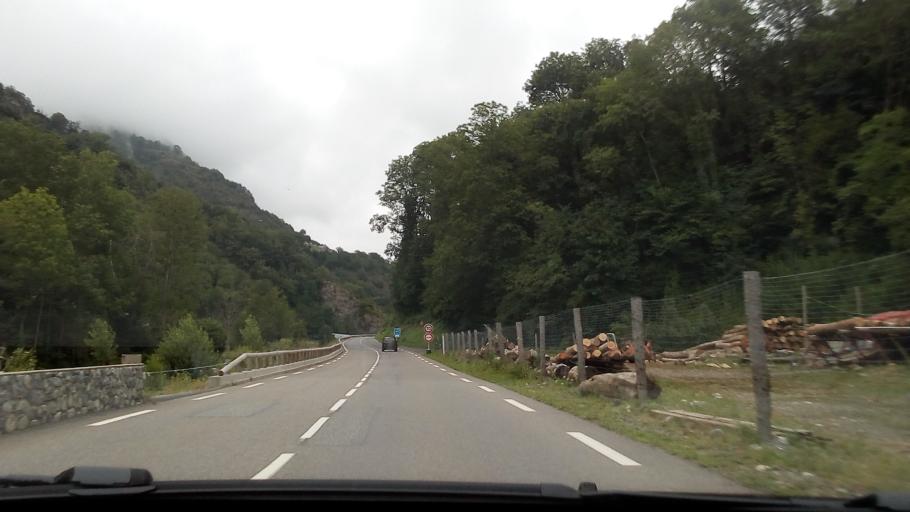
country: FR
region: Midi-Pyrenees
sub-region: Departement des Hautes-Pyrenees
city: Luz-Saint-Sauveur
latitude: 42.8770
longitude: 0.0097
